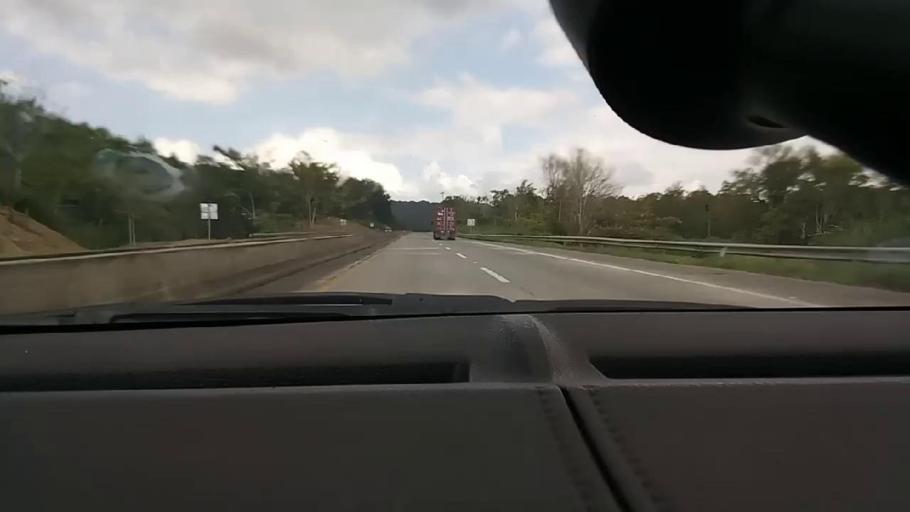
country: PA
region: Panama
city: Chilibre
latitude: 9.1446
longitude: -79.6289
